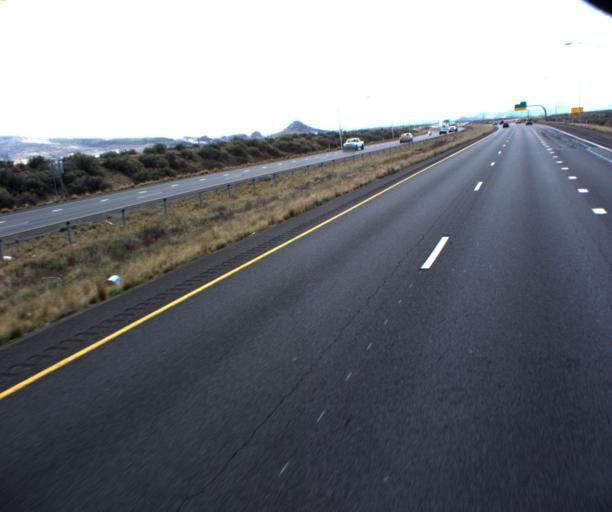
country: US
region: Arizona
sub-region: Yavapai County
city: Prescott Valley
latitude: 34.6341
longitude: -112.3462
